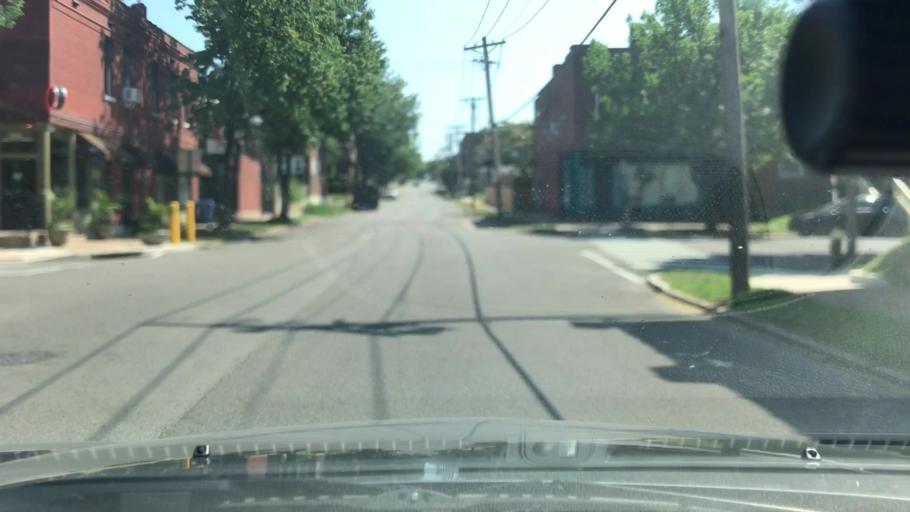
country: US
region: Missouri
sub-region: City of Saint Louis
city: St. Louis
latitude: 38.5999
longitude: -90.2501
